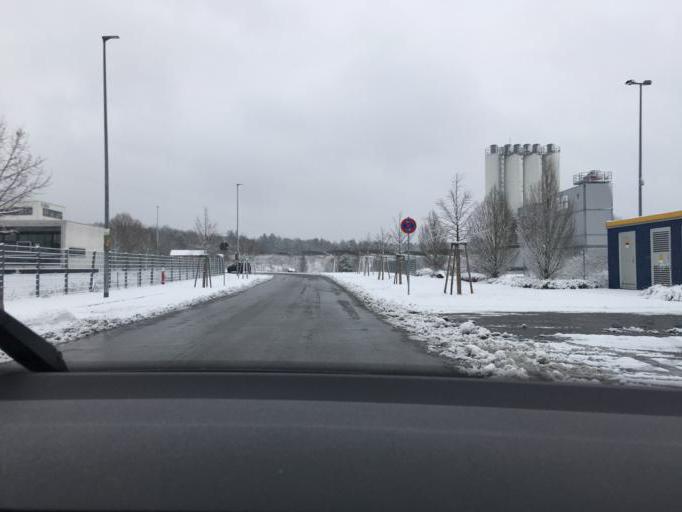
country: DE
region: Baden-Wuerttemberg
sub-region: Freiburg Region
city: Singen
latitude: 47.7596
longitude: 8.8892
